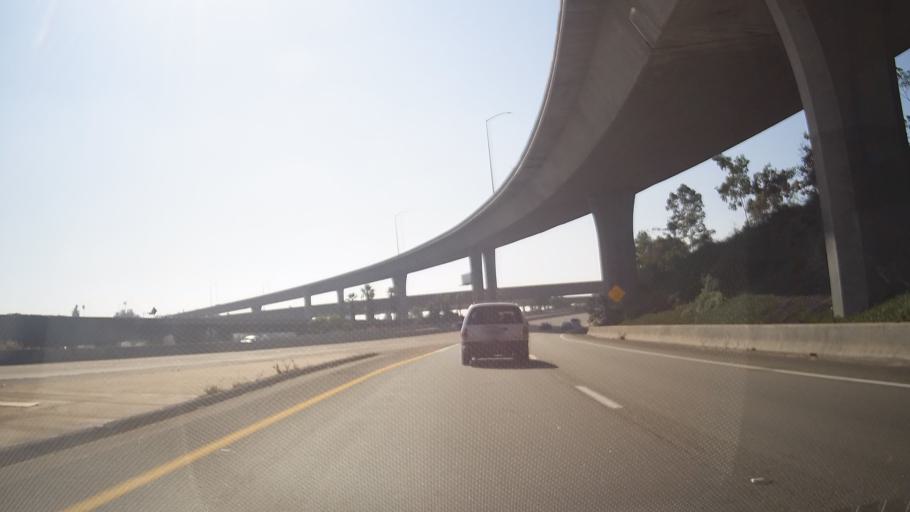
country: US
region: California
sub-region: San Diego County
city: Lemon Grove
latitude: 32.7494
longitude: -117.0173
